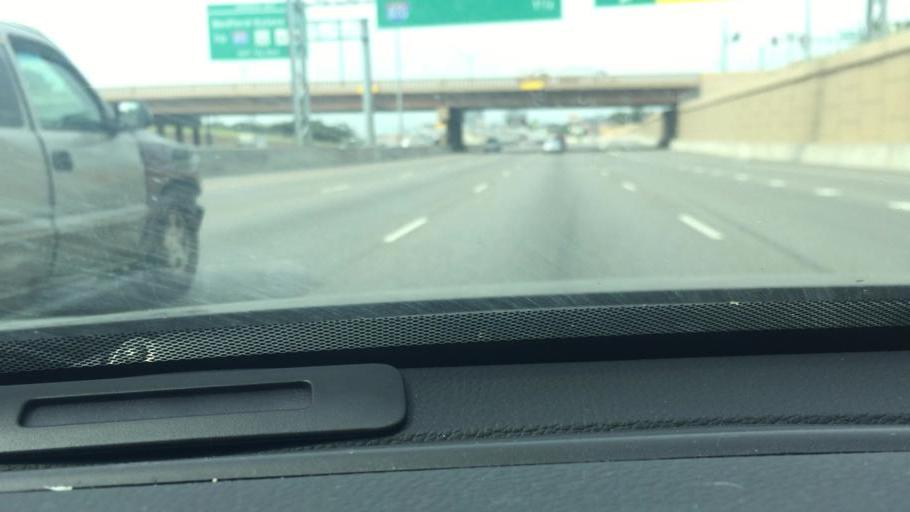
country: US
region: Texas
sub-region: Tarrant County
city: Hurst
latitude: 32.8401
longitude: -97.1769
